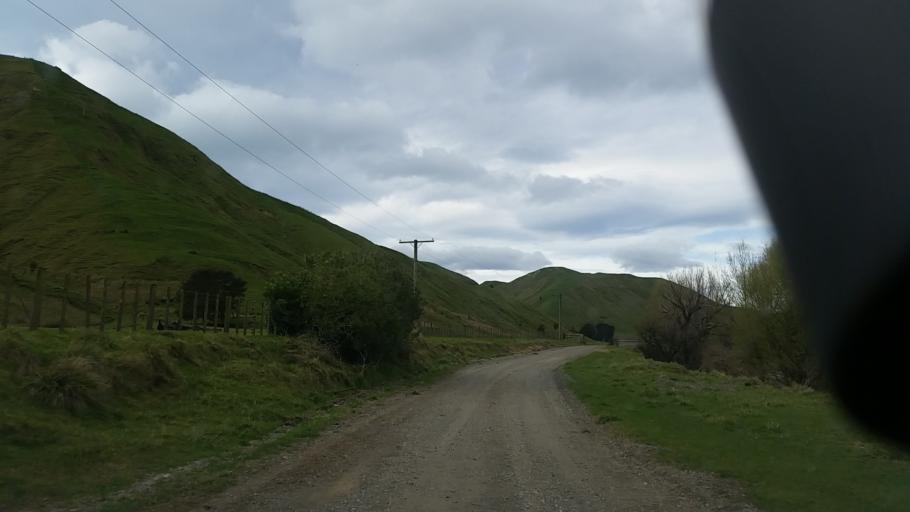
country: NZ
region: Hawke's Bay
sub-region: Napier City
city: Napier
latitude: -39.2694
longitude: 176.9830
